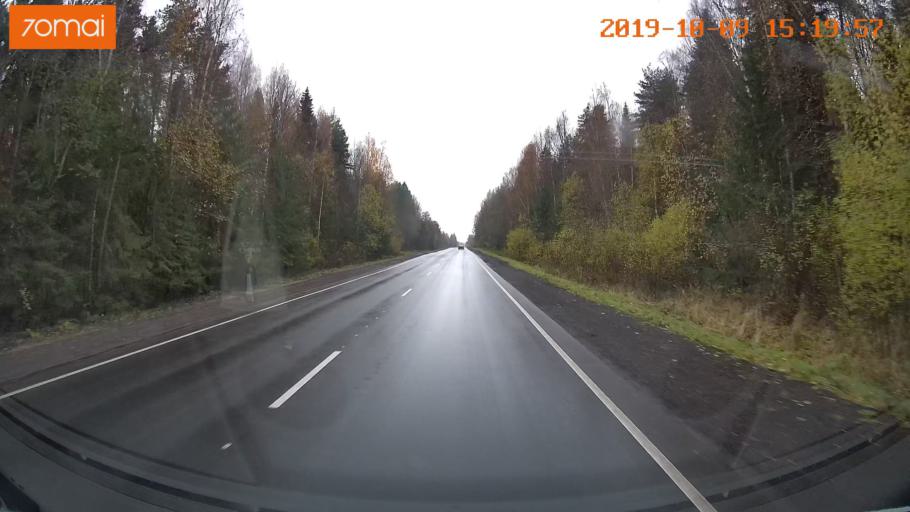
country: RU
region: Kostroma
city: Susanino
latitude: 58.0699
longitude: 41.5469
